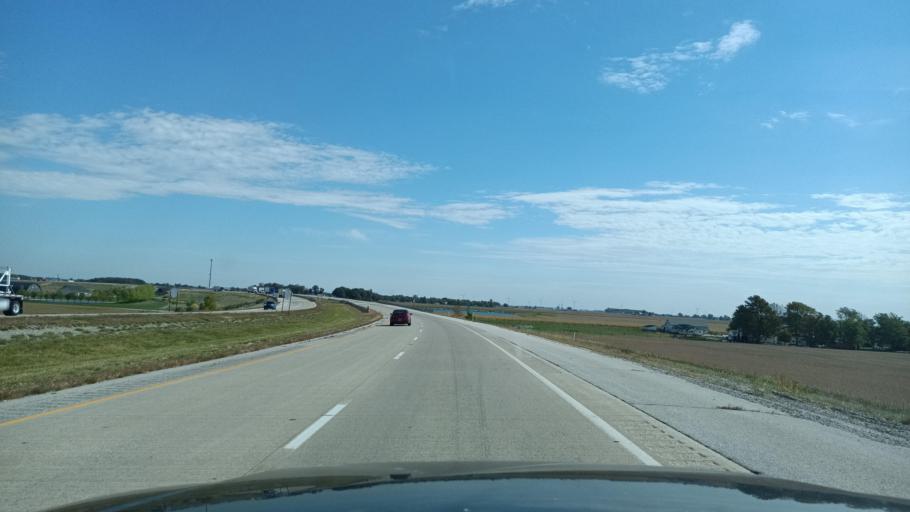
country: US
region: Indiana
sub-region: Allen County
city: Woodburn
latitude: 41.1215
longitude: -84.8900
